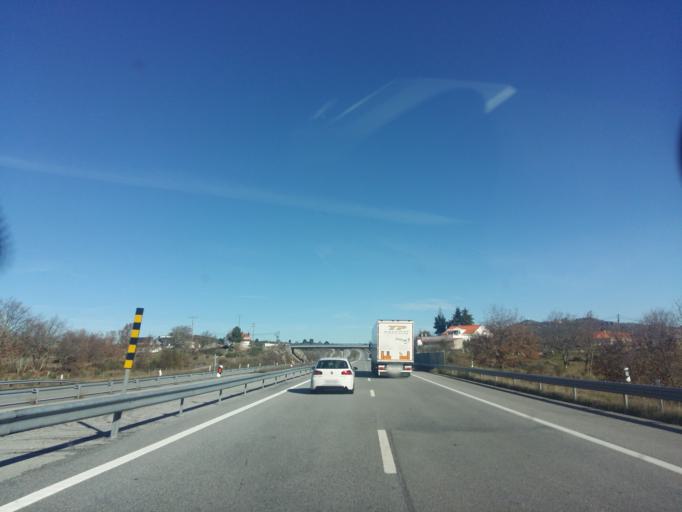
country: PT
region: Guarda
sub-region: Guarda
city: Sequeira
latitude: 40.5844
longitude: -7.1530
